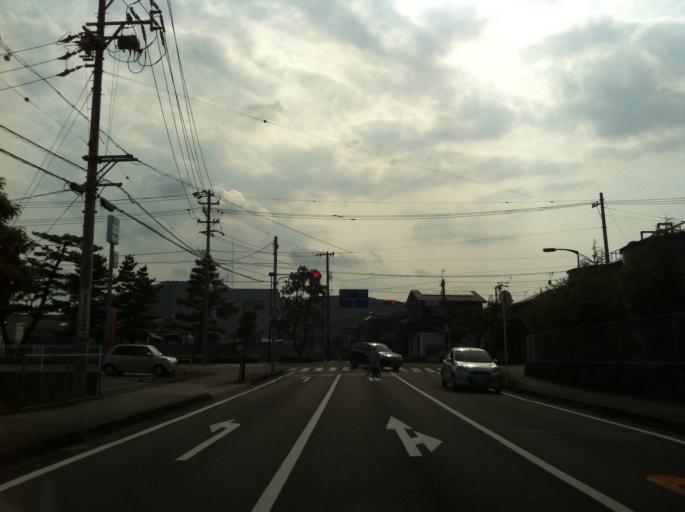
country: JP
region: Shizuoka
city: Fujieda
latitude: 34.9056
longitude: 138.2832
